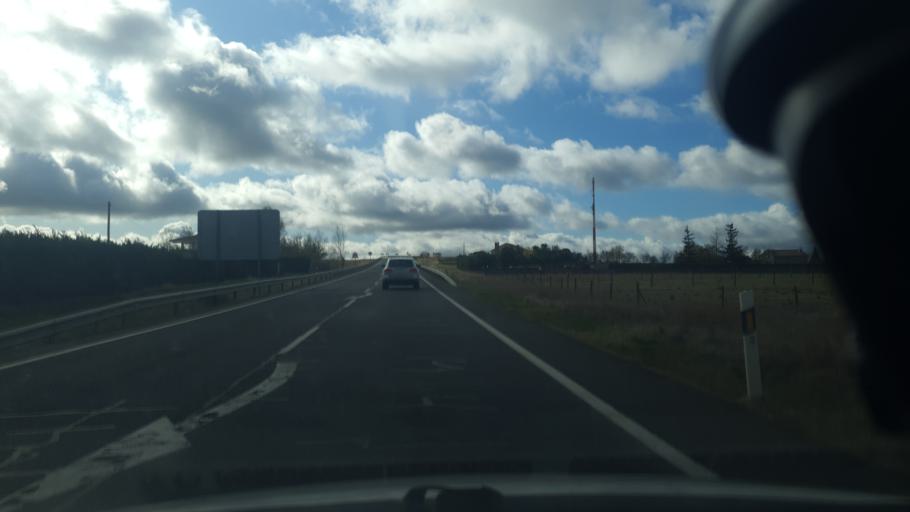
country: ES
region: Castille and Leon
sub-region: Provincia de Segovia
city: Otero de Herreros
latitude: 40.8736
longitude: -4.2241
